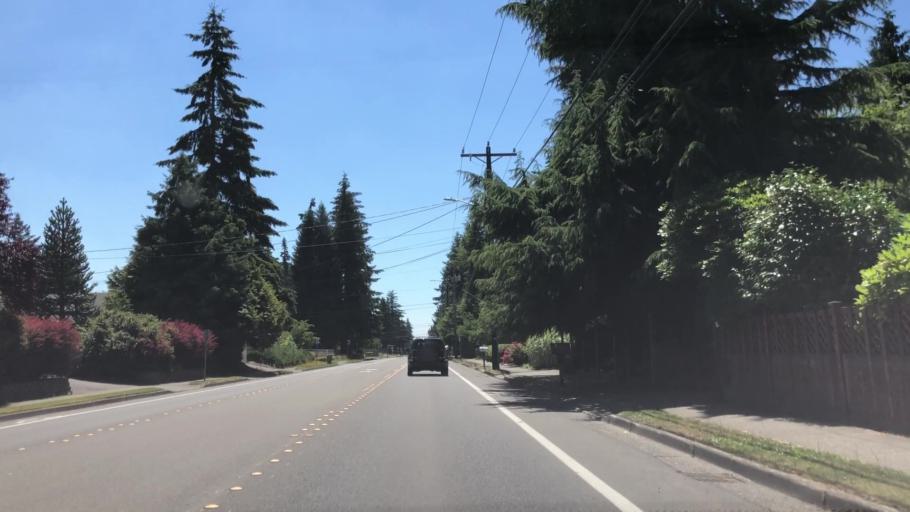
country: US
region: Washington
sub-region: Snohomish County
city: Alderwood Manor
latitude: 47.8383
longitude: -122.2925
